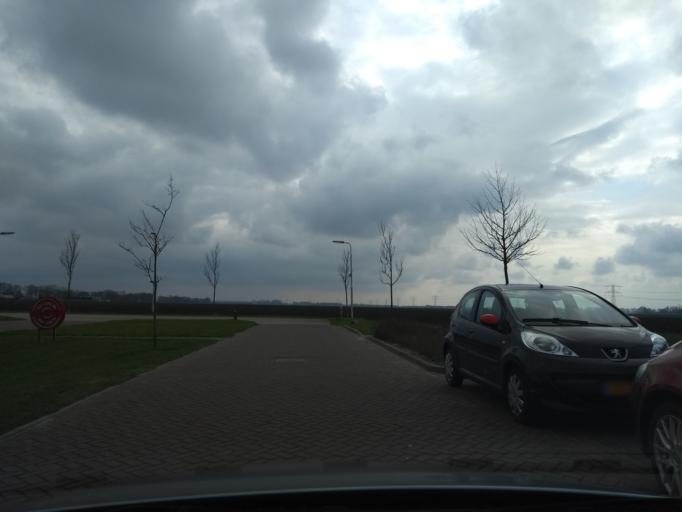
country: NL
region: Flevoland
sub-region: Gemeente Noordoostpolder
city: Ens
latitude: 52.7397
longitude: 5.8516
